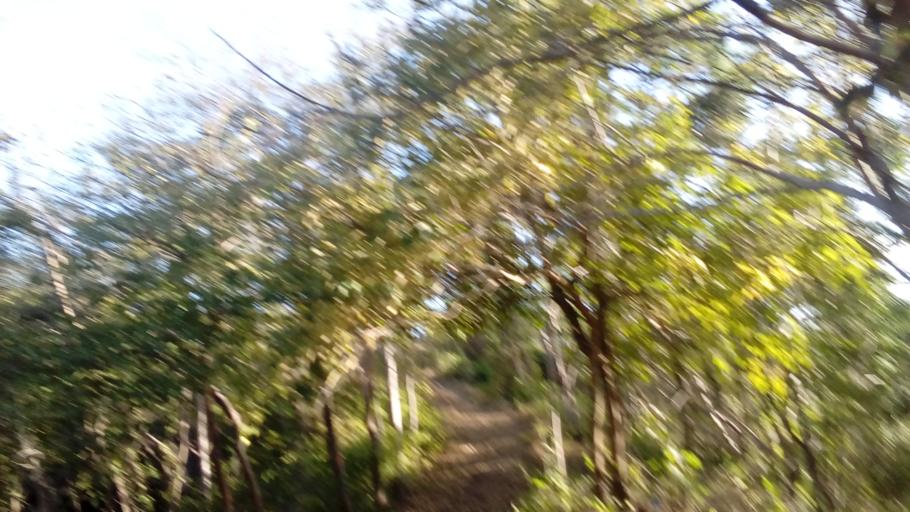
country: CR
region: Guanacaste
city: Sardinal
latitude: 10.3954
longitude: -85.8333
